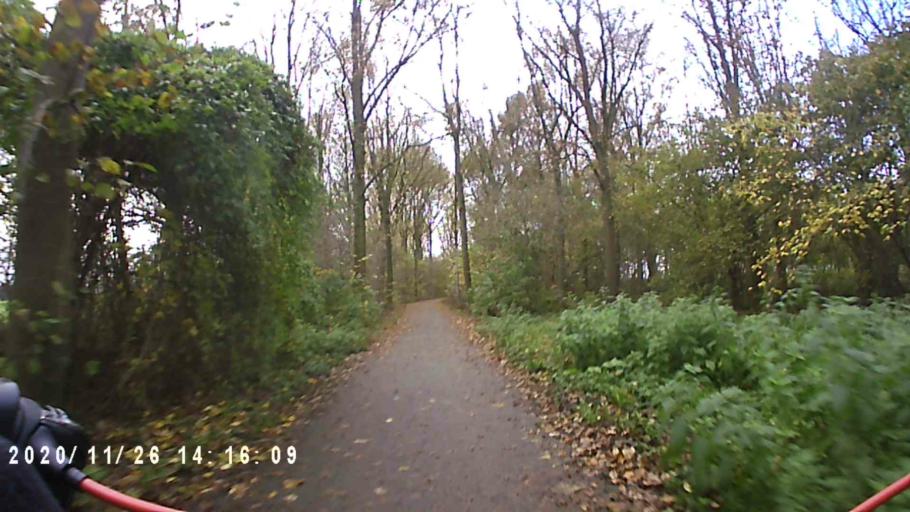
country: NL
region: Groningen
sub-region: Gemeente Appingedam
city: Appingedam
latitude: 53.3281
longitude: 6.8853
